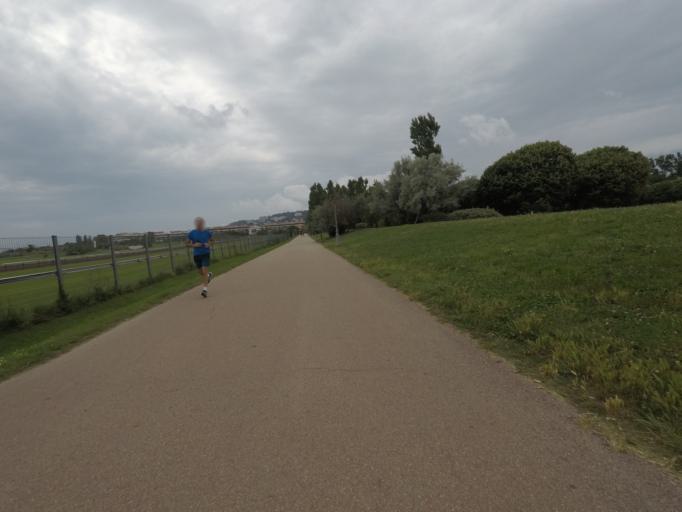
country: FR
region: Provence-Alpes-Cote d'Azur
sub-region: Departement des Bouches-du-Rhone
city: Marseille 08
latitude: 43.2577
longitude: 5.3810
